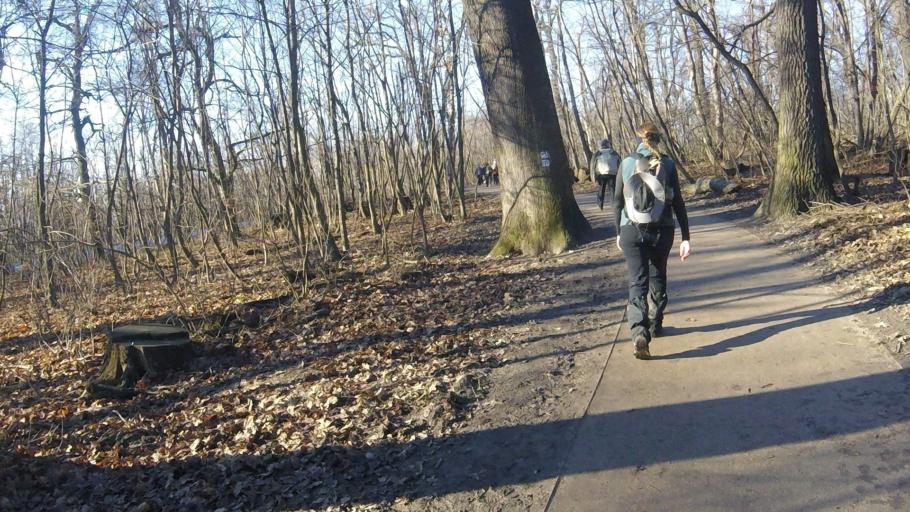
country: HU
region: Pest
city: Budakeszi
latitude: 47.5083
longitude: 18.9587
